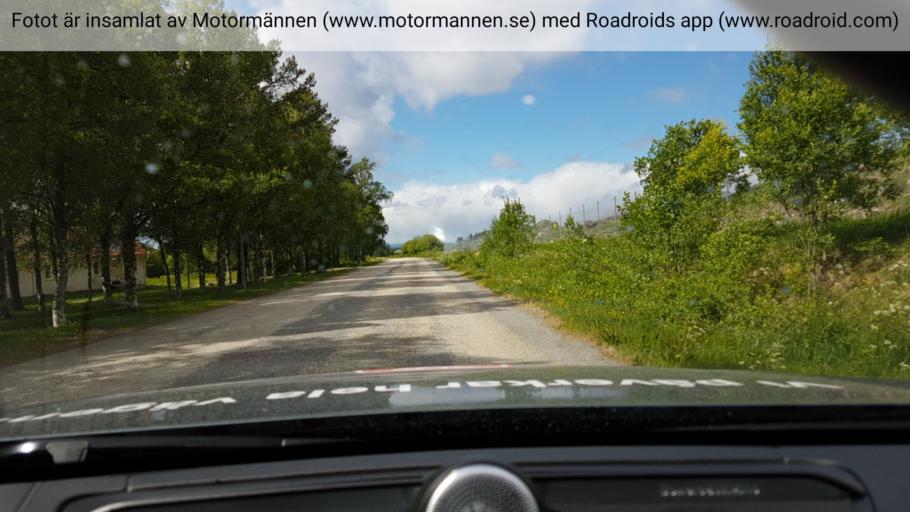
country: SE
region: Jaemtland
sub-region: Krokoms Kommun
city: Krokom
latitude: 63.1977
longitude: 14.4757
